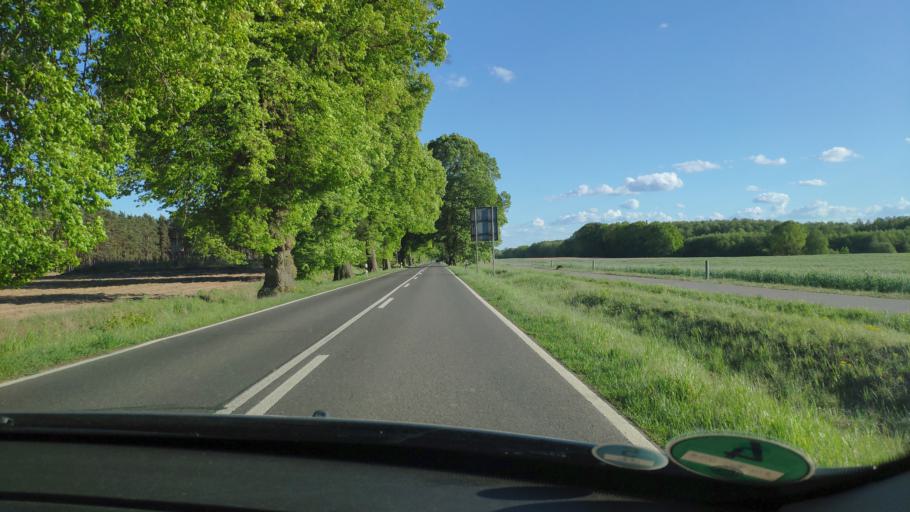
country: DE
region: Mecklenburg-Vorpommern
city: Rechlin
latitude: 53.2983
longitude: 12.8123
